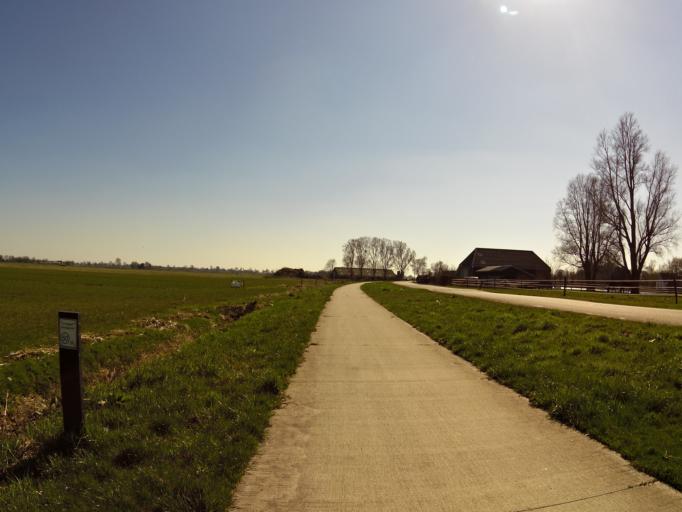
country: NL
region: Overijssel
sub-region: Gemeente Steenwijkerland
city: Blokzijl
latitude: 52.7596
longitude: 5.9960
